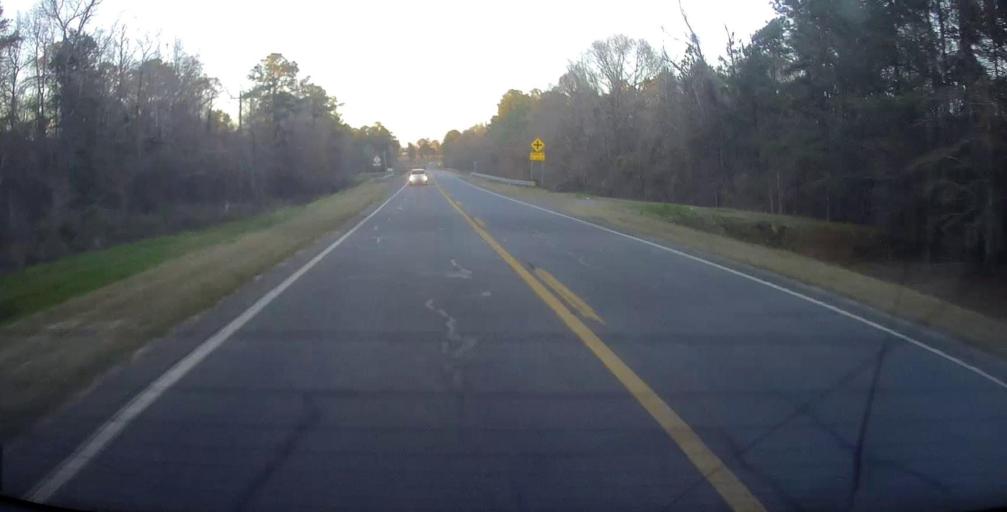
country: US
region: Georgia
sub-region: Dodge County
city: Eastman
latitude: 32.2533
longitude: -83.1409
